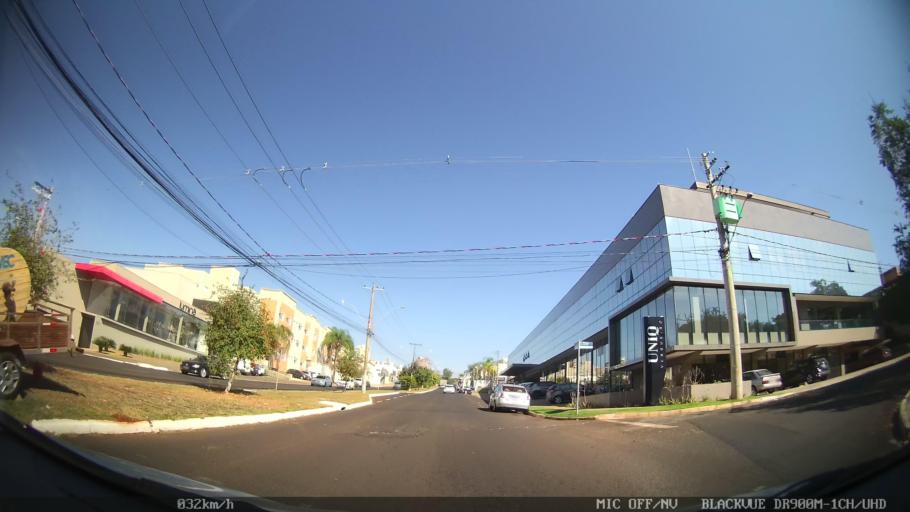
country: BR
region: Sao Paulo
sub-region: Ribeirao Preto
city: Ribeirao Preto
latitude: -21.1995
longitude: -47.8011
